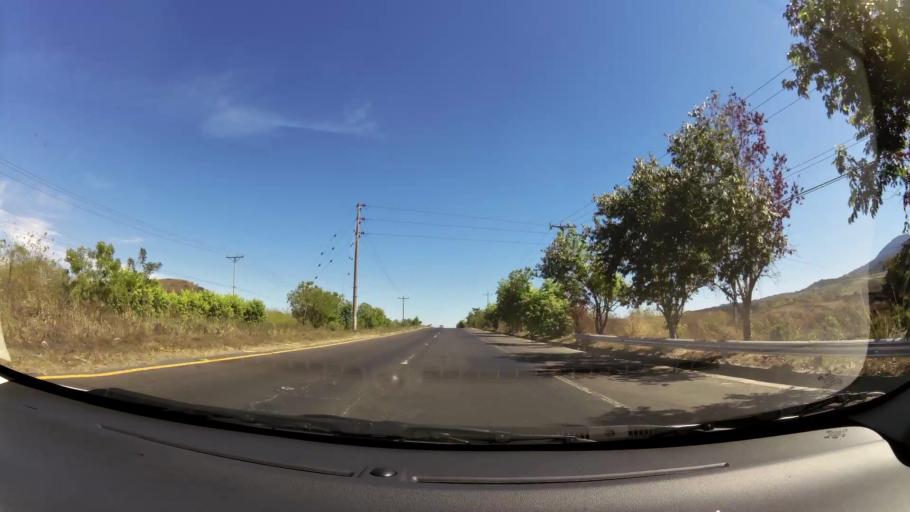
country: SV
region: La Libertad
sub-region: Distrito de Quezaltepeque
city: Quezaltepeque
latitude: 13.7991
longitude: -89.3392
